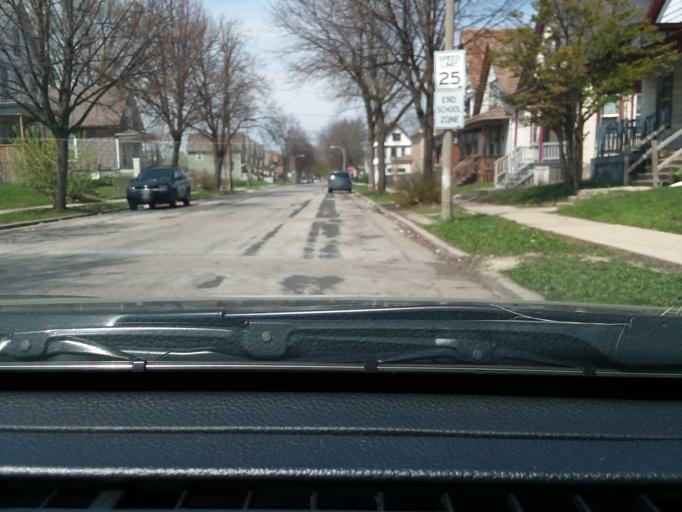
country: US
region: Wisconsin
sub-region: Milwaukee County
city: Milwaukee
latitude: 43.0686
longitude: -87.9254
